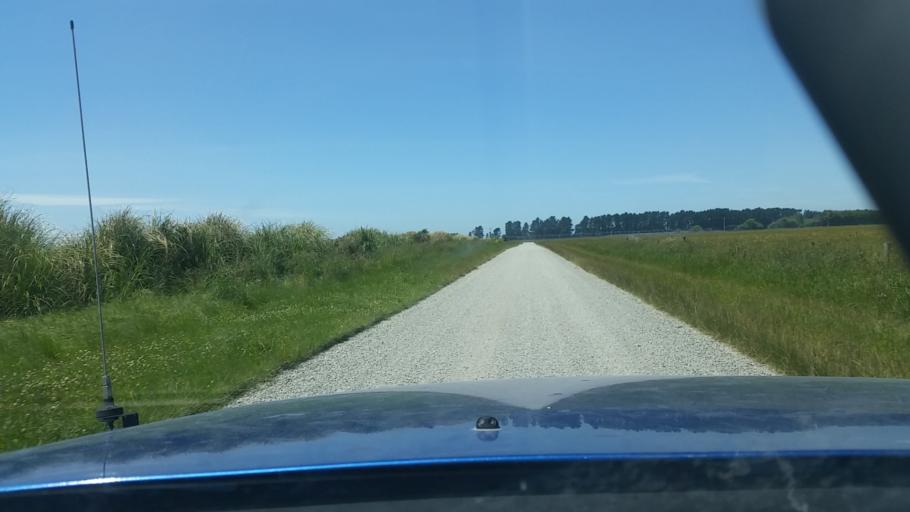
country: NZ
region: Canterbury
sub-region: Ashburton District
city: Tinwald
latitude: -43.9728
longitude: 171.7481
